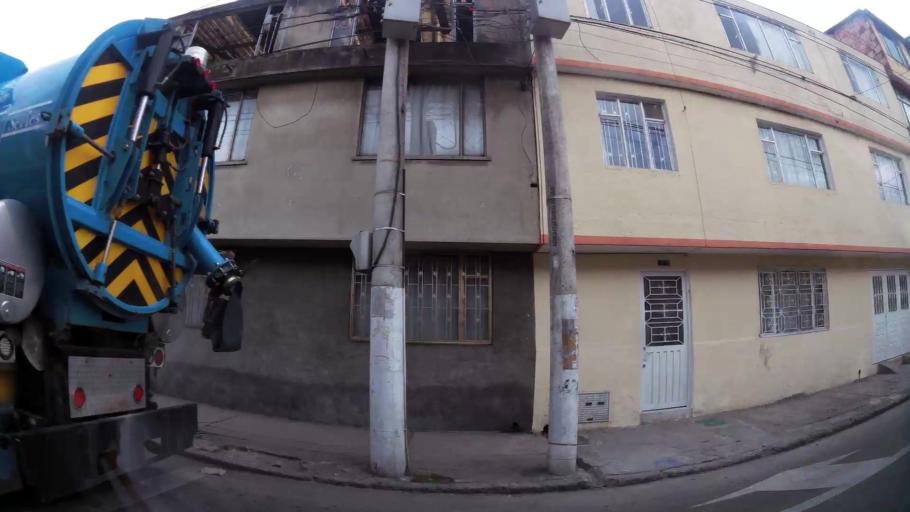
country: CO
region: Bogota D.C.
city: Bogota
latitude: 4.6731
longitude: -74.1005
